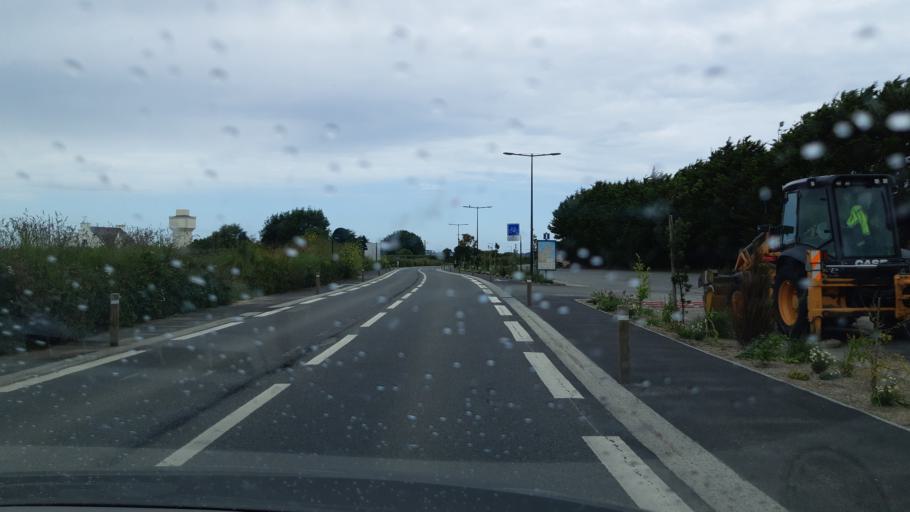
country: FR
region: Brittany
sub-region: Departement du Finistere
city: Roscoff
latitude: 48.7097
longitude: -3.9838
